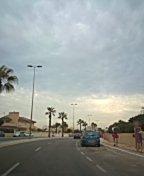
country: ES
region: Murcia
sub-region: Murcia
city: La Manga del Mar Menor
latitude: 37.7125
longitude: -0.7421
